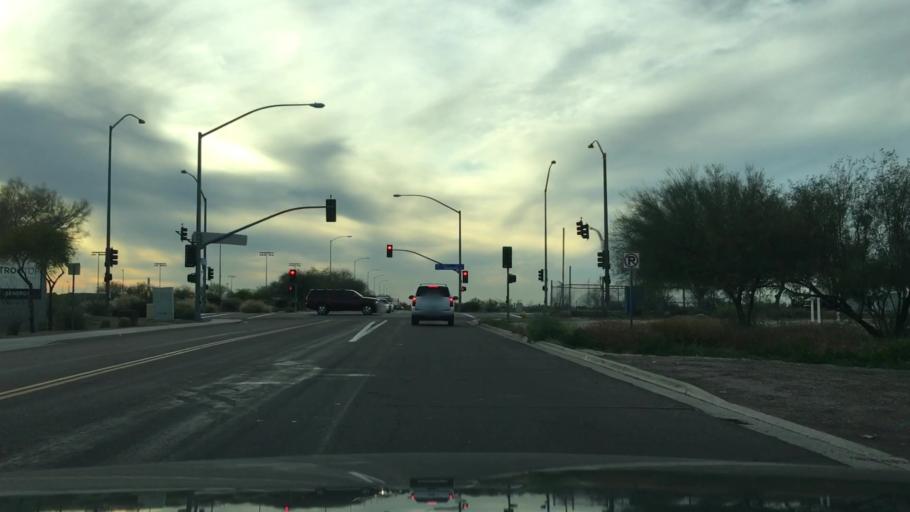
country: US
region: Arizona
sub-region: Maricopa County
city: Mesa
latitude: 33.4775
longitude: -111.7350
